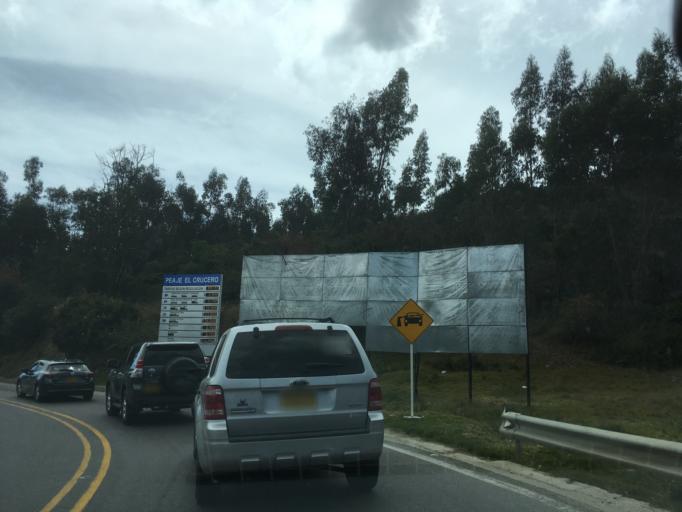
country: CO
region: Boyaca
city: Firavitoba
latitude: 5.6331
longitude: -72.9220
